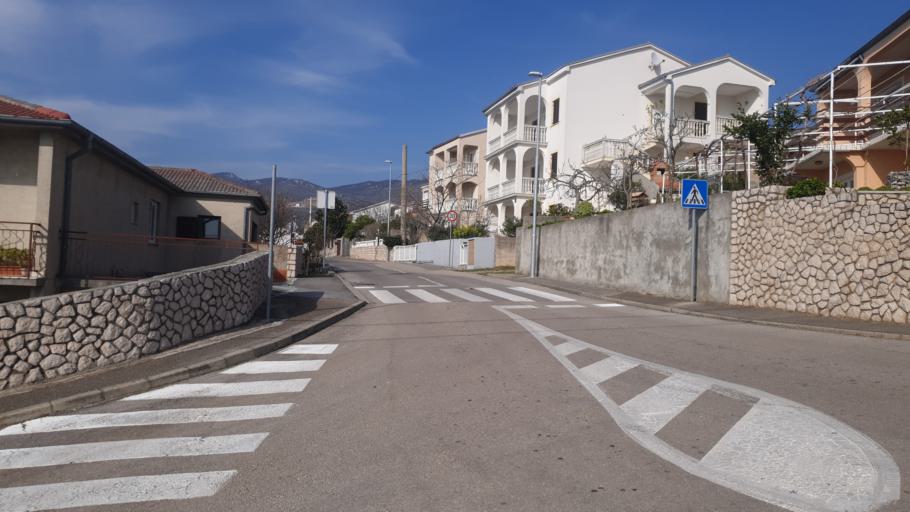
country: HR
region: Primorsko-Goranska
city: Novi Vinodolski
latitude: 45.1293
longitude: 14.7952
